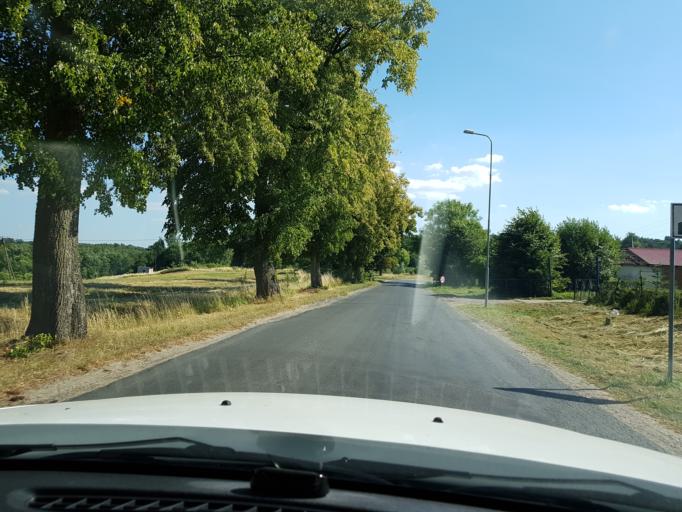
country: PL
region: West Pomeranian Voivodeship
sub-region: Powiat bialogardzki
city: Karlino
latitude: 53.9603
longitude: 15.9003
